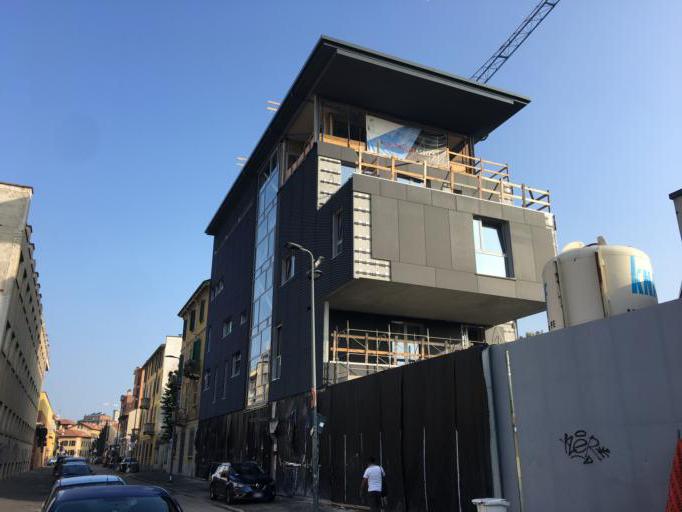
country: IT
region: Lombardy
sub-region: Citta metropolitana di Milano
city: Bresso
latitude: 45.5051
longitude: 9.2085
